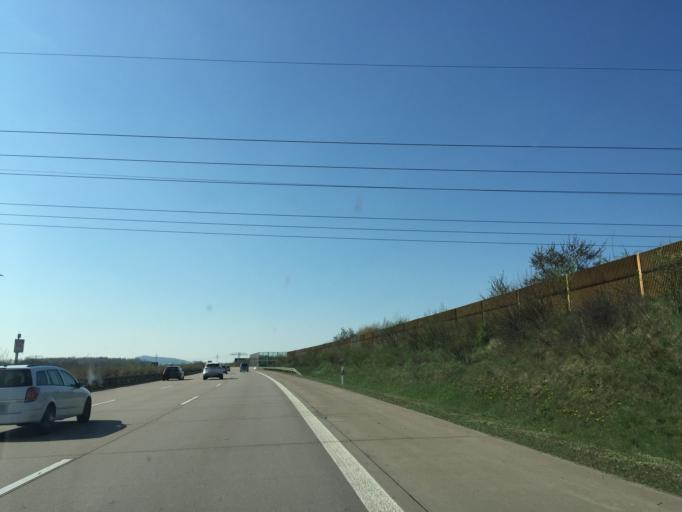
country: DE
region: Thuringia
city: Horselgau
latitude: 50.9158
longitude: 10.5804
